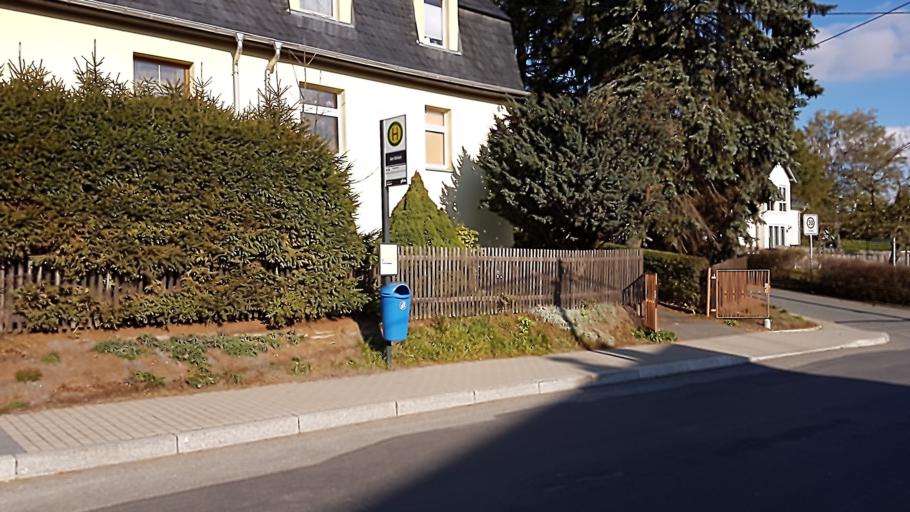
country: DE
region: Saxony
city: Gornau
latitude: 50.7847
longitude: 13.0002
